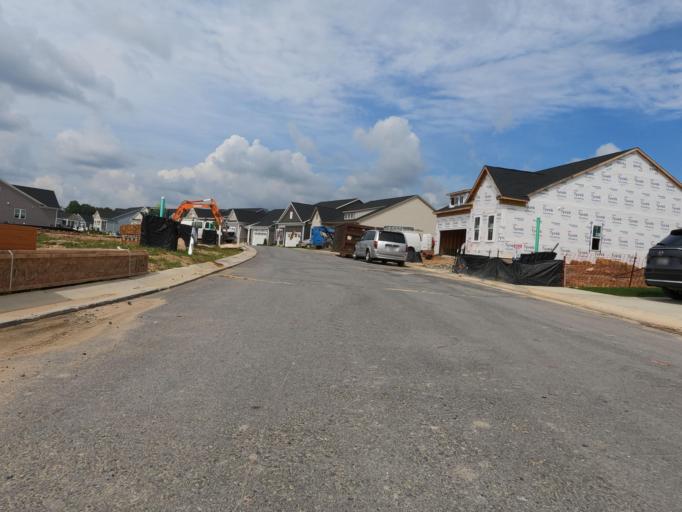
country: US
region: Maryland
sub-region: Anne Arundel County
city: Crofton
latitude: 39.0249
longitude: -76.7293
